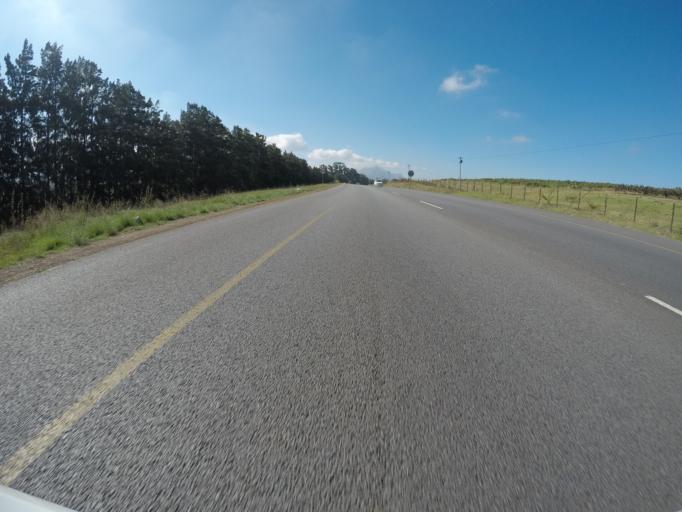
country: ZA
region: Western Cape
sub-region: Cape Winelands District Municipality
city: Stellenbosch
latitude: -33.8794
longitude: 18.8161
